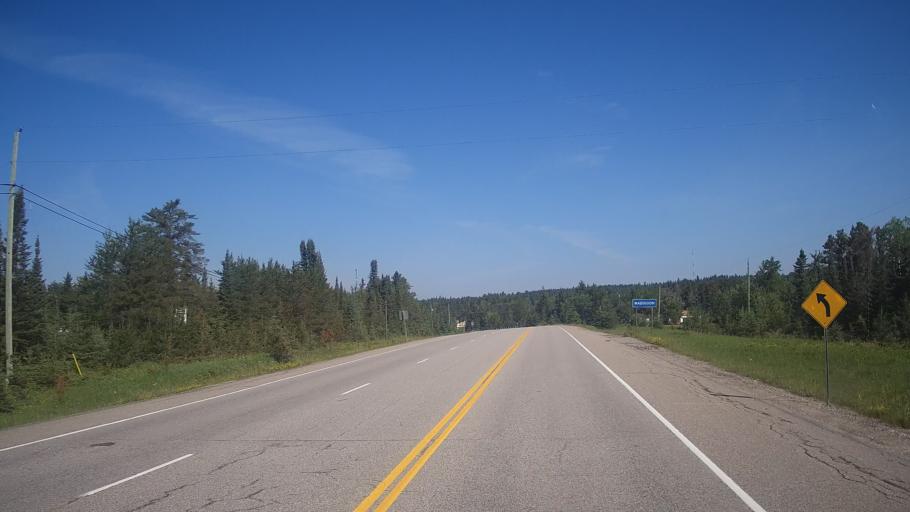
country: CA
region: Ontario
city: Dryden
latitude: 49.7161
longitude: -92.5949
